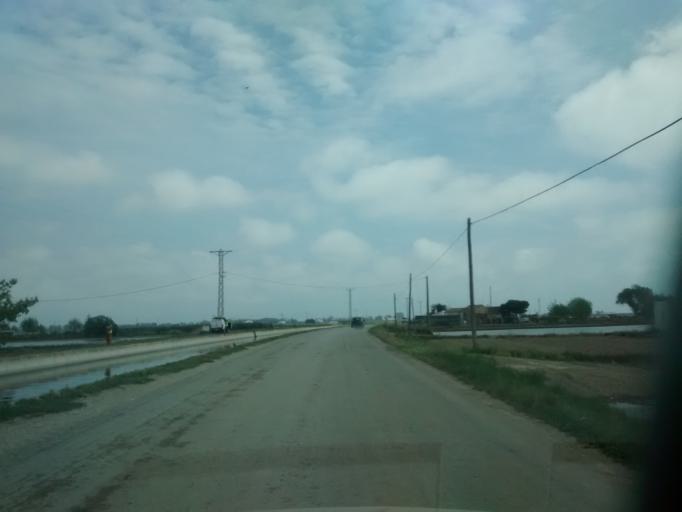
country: ES
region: Catalonia
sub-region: Provincia de Tarragona
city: Deltebre
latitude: 40.7025
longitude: 0.7368
